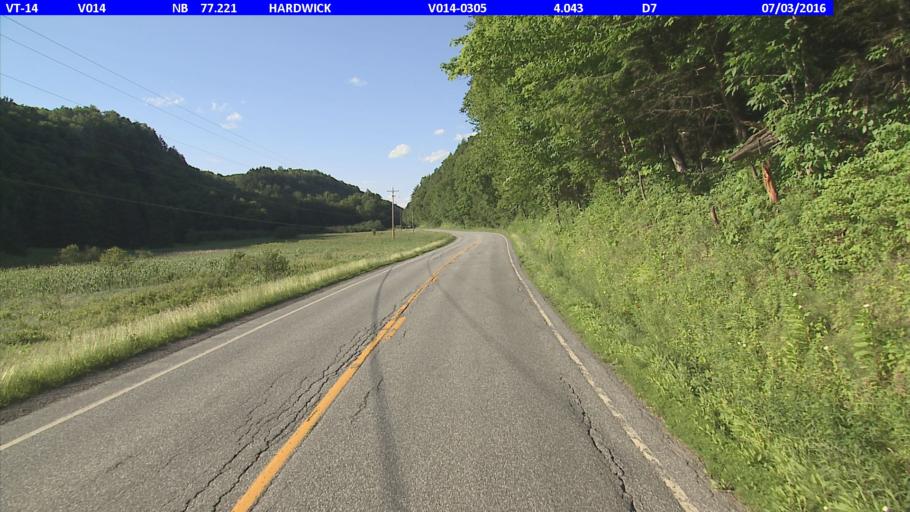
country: US
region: Vermont
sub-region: Caledonia County
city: Hardwick
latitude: 44.5518
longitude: -72.3698
